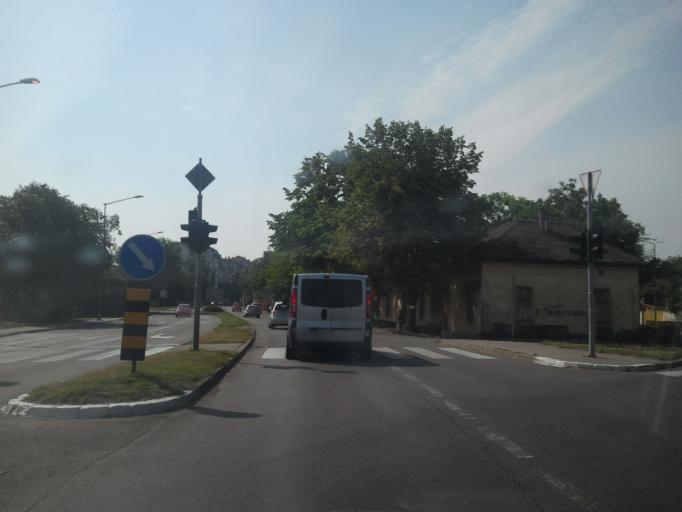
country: RS
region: Autonomna Pokrajina Vojvodina
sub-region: Juznobacki Okrug
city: Petrovaradin
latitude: 45.2426
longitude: 19.8822
